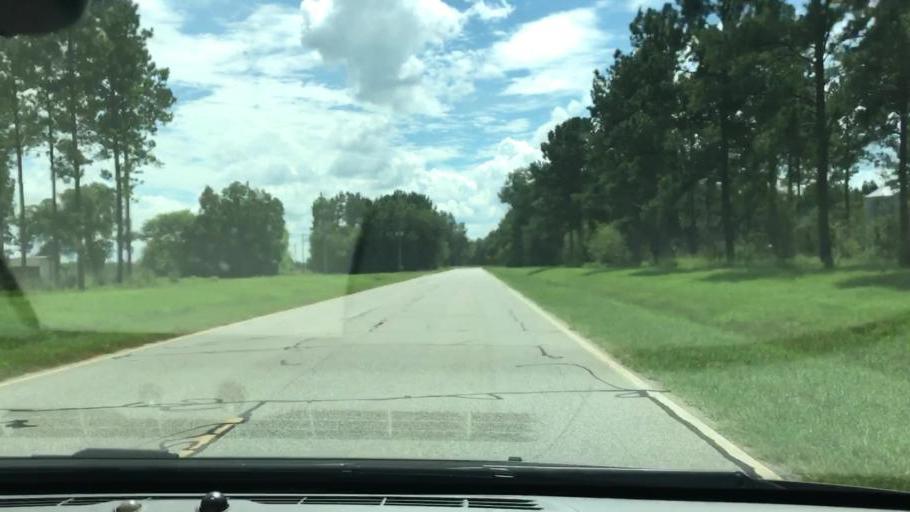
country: US
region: Georgia
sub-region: Quitman County
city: Georgetown
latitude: 32.0512
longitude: -85.0364
